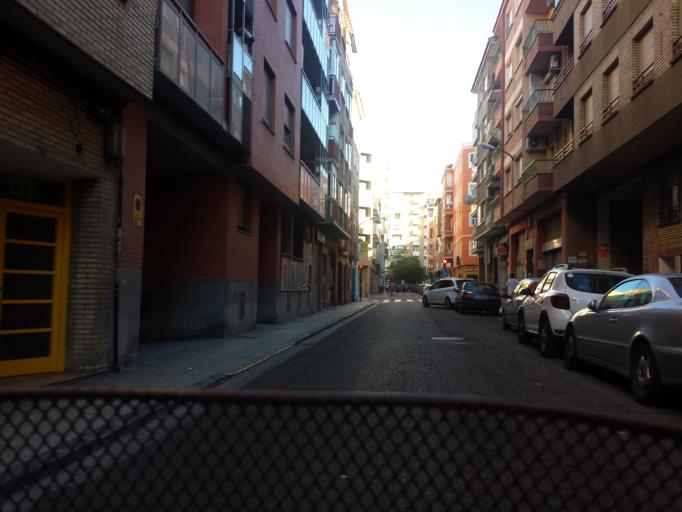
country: ES
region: Aragon
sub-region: Provincia de Zaragoza
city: Delicias
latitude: 41.6544
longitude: -0.9071
